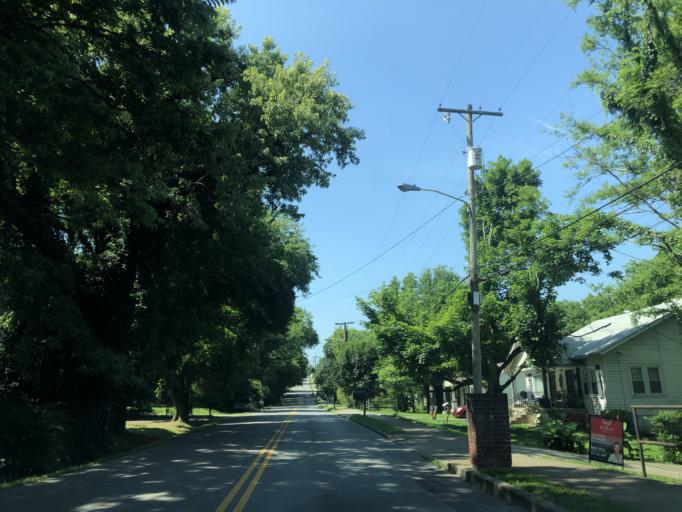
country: US
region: Tennessee
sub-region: Davidson County
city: Nashville
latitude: 36.2045
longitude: -86.7659
